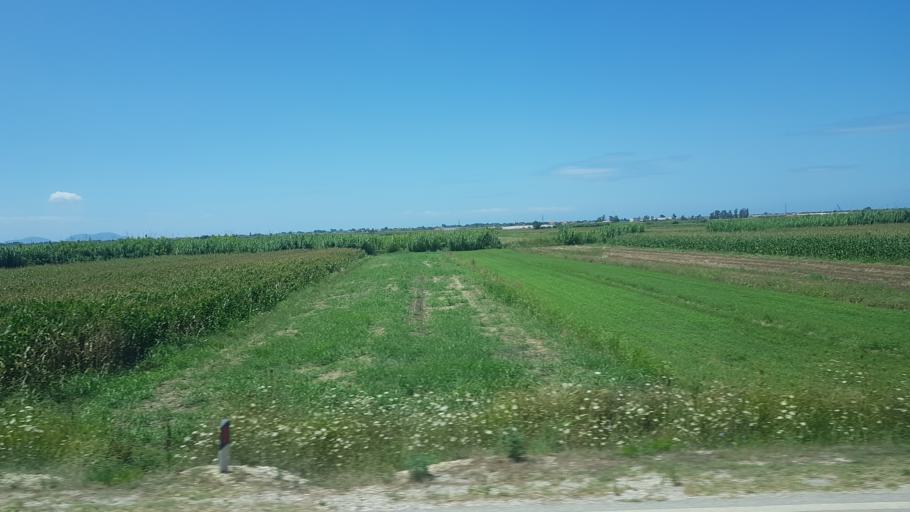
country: AL
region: Fier
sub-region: Rrethi i Fierit
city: Frakulla e Madhe
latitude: 40.6576
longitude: 19.4905
